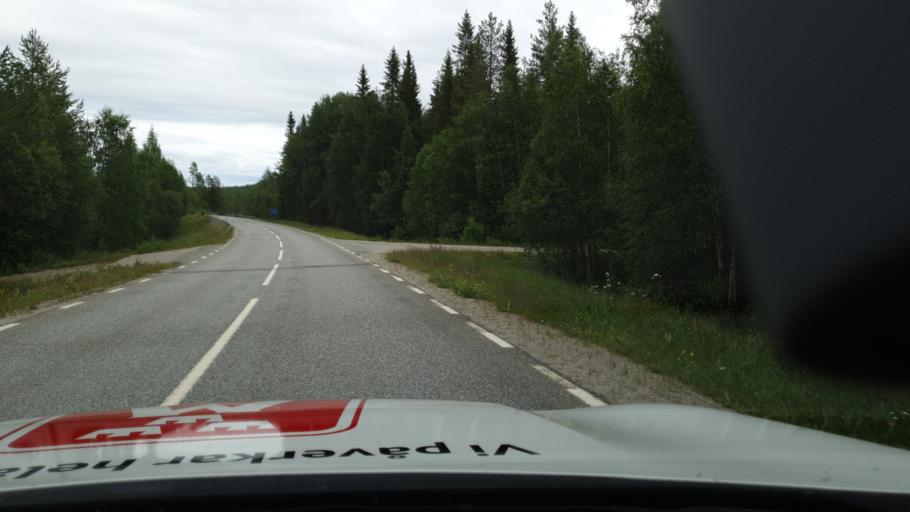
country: SE
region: Vaesterbotten
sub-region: Lycksele Kommun
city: Soderfors
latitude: 64.6326
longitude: 18.0012
